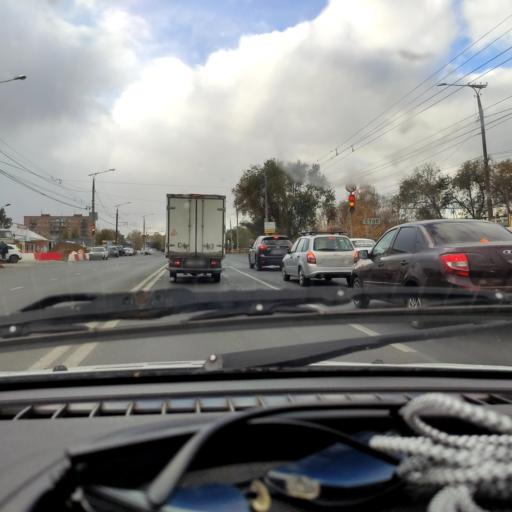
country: RU
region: Samara
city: Zhigulevsk
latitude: 53.4865
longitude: 49.4918
